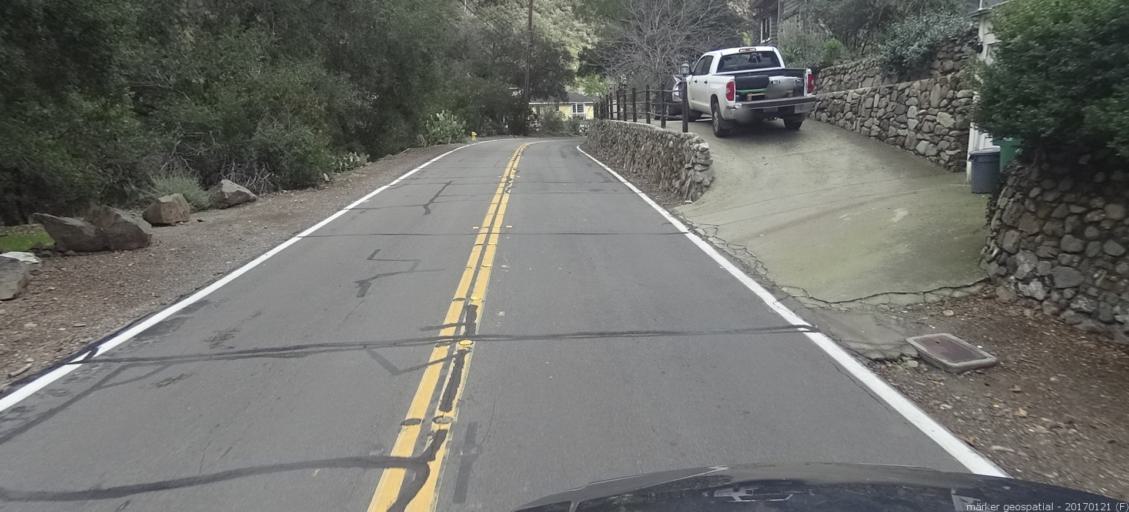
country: US
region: California
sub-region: Orange County
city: Portola Hills
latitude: 33.7474
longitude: -117.6147
